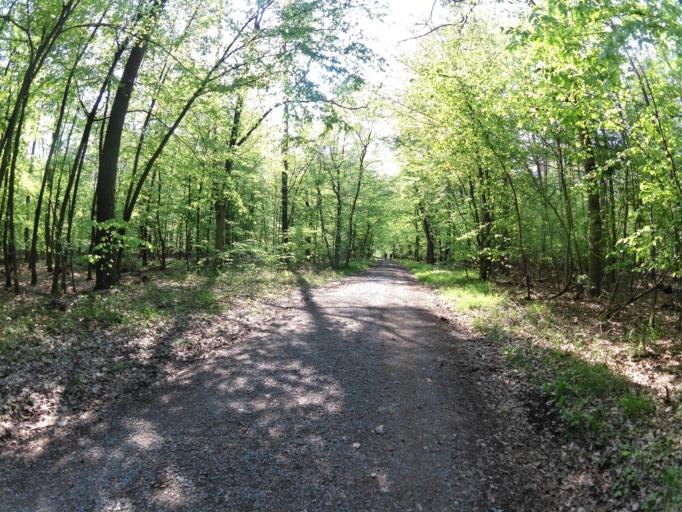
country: DE
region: Bavaria
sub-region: Regierungsbezirk Unterfranken
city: Sommerhausen
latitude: 49.7061
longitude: 10.0516
